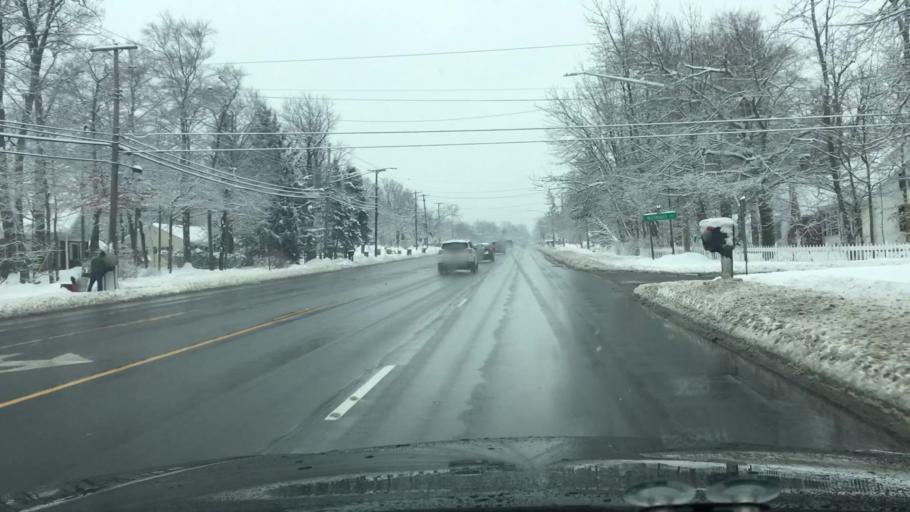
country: US
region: New York
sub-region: Erie County
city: Orchard Park
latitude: 42.8157
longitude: -78.7524
